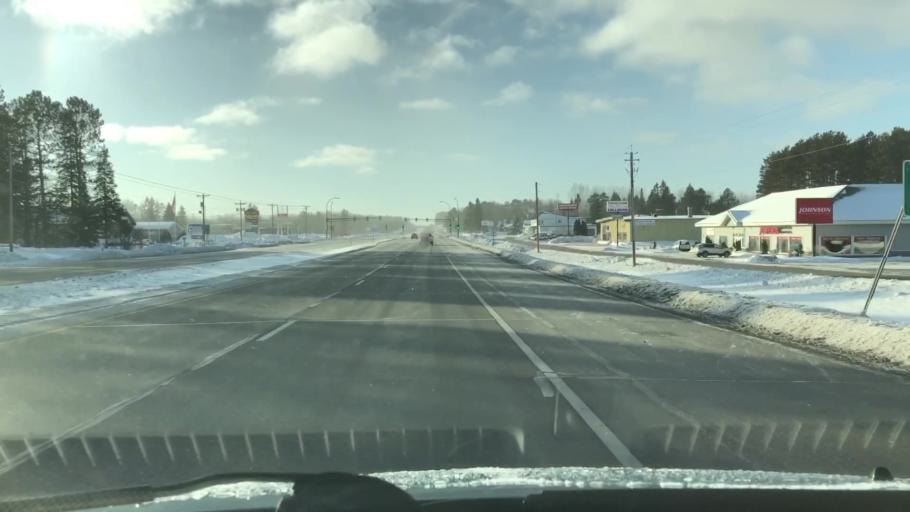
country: US
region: Minnesota
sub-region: Saint Louis County
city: Hermantown
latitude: 46.8368
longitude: -92.2137
